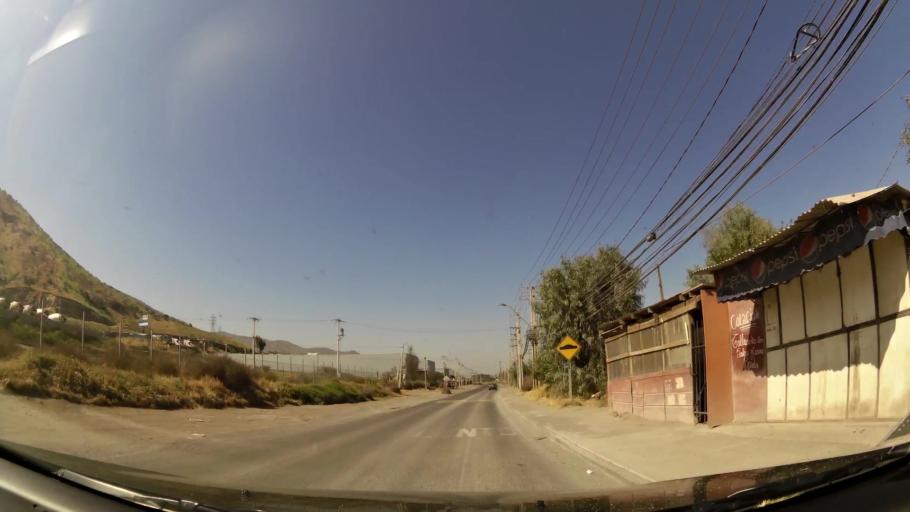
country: CL
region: Santiago Metropolitan
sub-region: Provincia de Chacabuco
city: Chicureo Abajo
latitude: -33.3215
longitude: -70.7088
